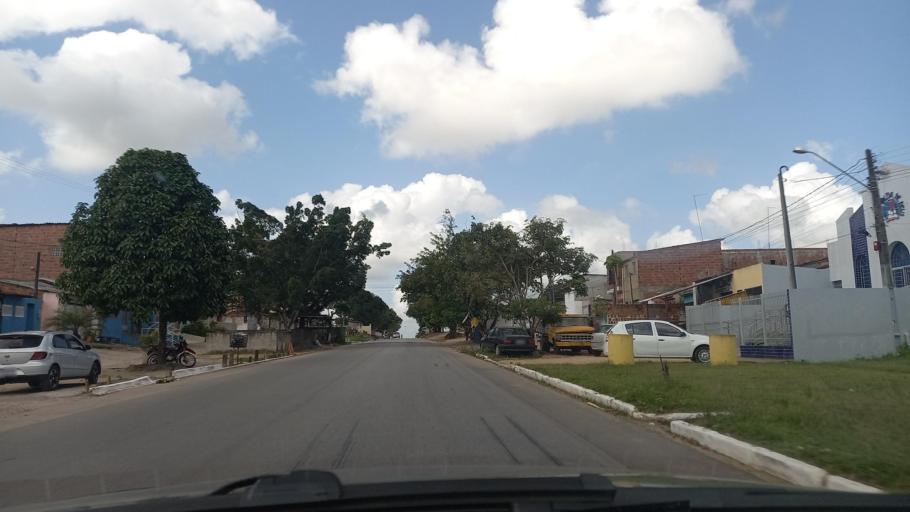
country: BR
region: Pernambuco
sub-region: Goiana
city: Goiana
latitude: -7.5698
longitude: -35.0264
